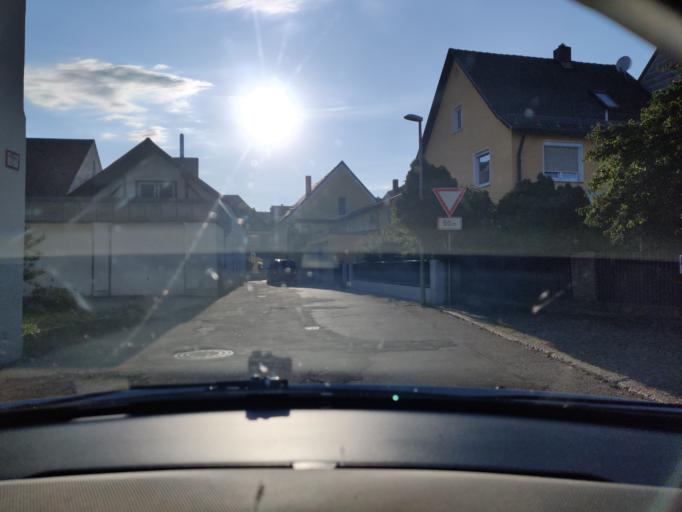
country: DE
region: Bavaria
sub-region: Upper Palatinate
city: Nabburg
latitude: 49.4534
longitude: 12.1860
